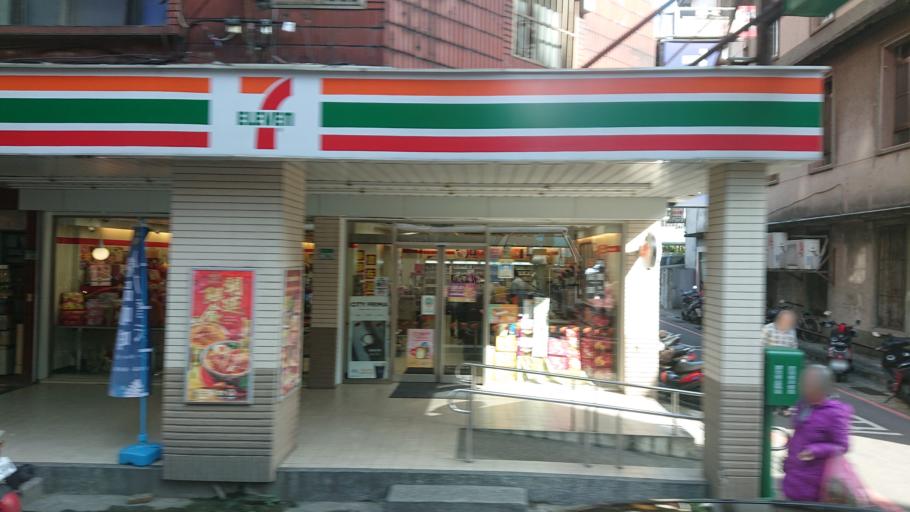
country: TW
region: Taiwan
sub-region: Keelung
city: Keelung
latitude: 25.1079
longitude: 121.8071
